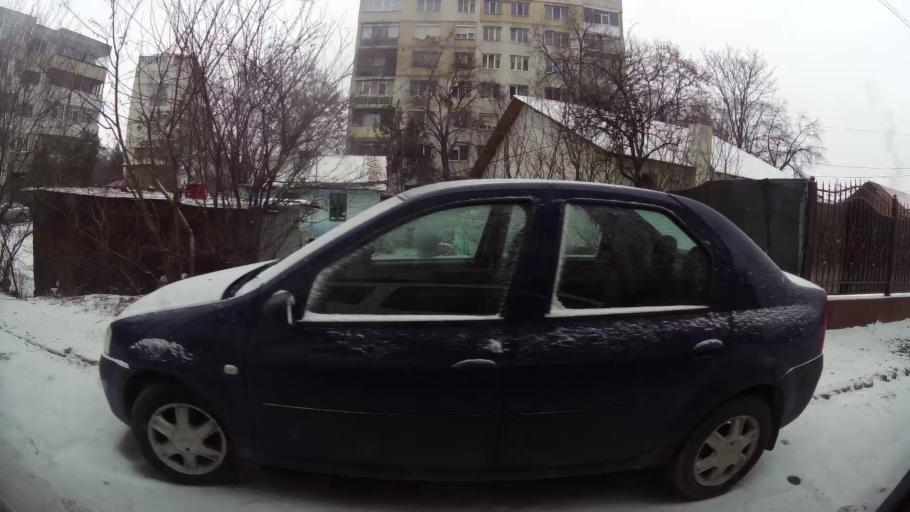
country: RO
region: Prahova
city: Ploiesti
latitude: 44.9531
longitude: 26.0125
